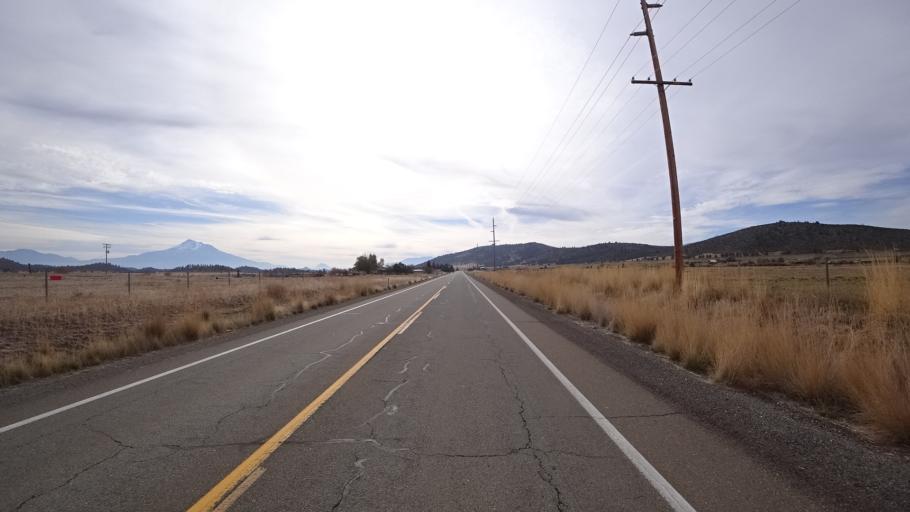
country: US
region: California
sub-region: Siskiyou County
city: Montague
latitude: 41.6964
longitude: -122.5351
